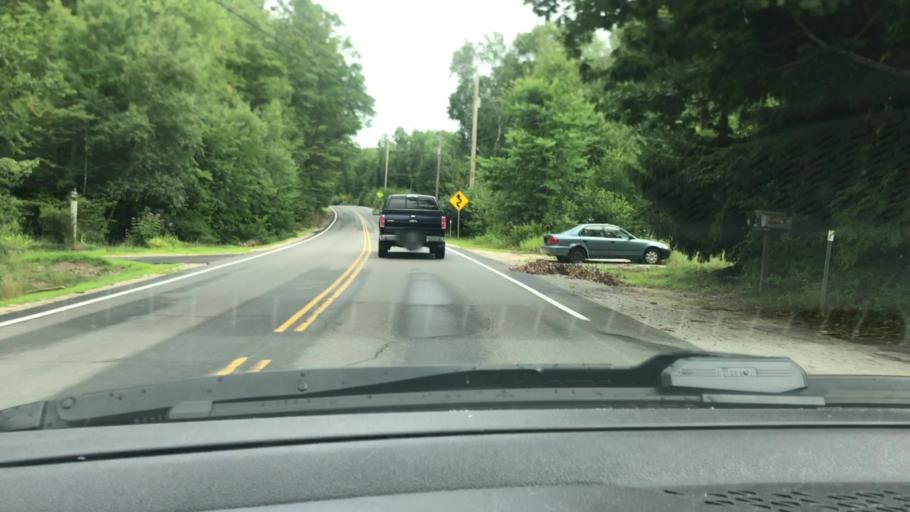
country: US
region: New Hampshire
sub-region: Merrimack County
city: Epsom
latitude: 43.2193
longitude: -71.2910
